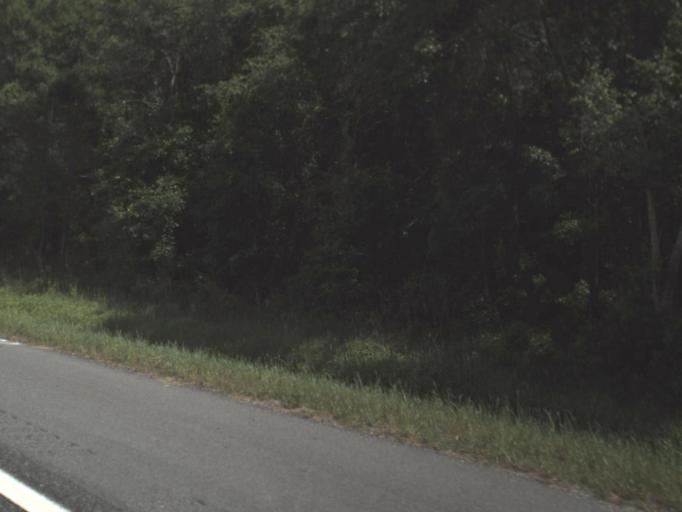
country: US
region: Florida
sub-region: Columbia County
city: Five Points
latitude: 30.2452
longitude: -82.6935
